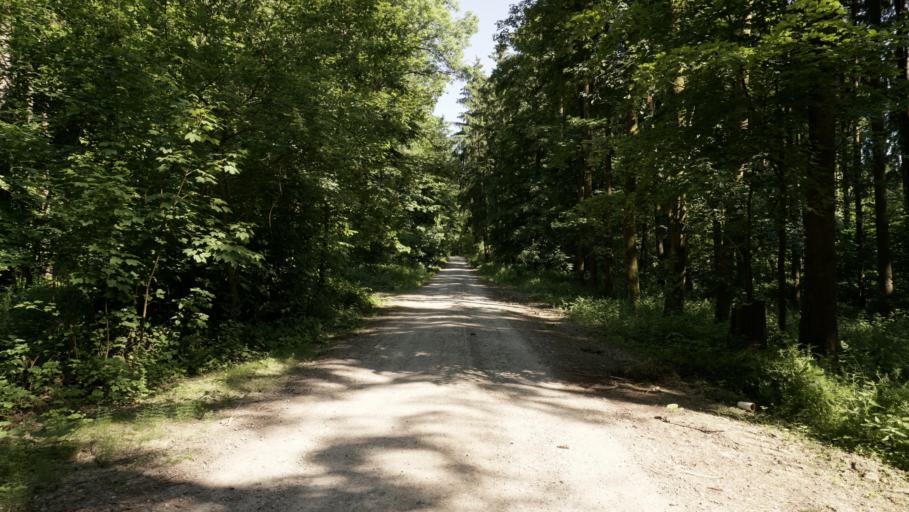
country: DE
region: Baden-Wuerttemberg
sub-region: Karlsruhe Region
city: Mosbach
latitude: 49.3387
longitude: 9.1911
